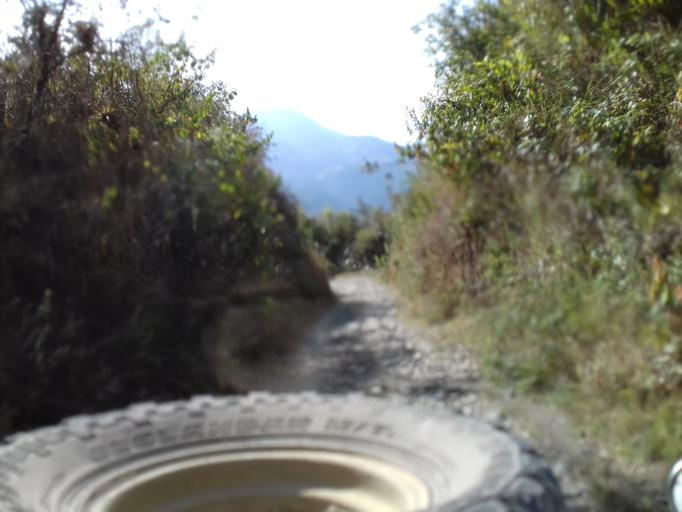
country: CO
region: Tolima
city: Cajamarca
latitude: 4.5322
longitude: -75.4179
